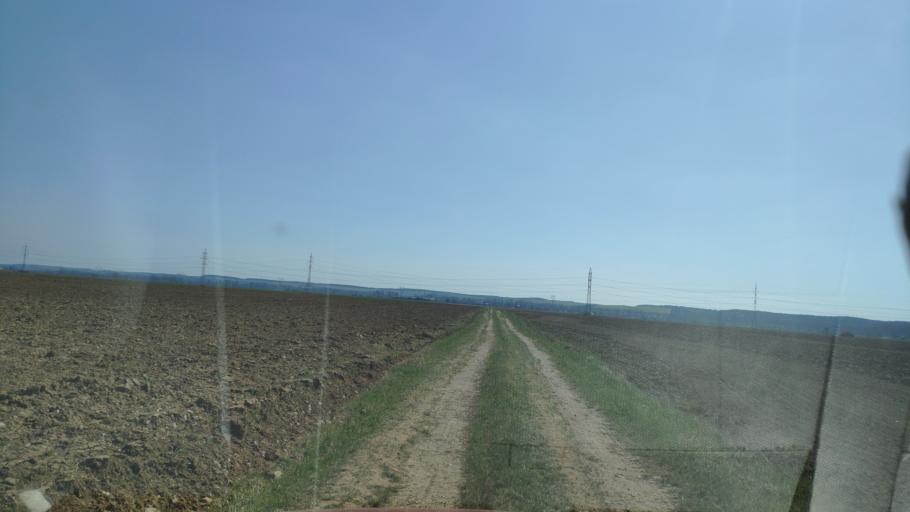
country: SK
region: Kosicky
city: Moldava nad Bodvou
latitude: 48.6023
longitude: 20.9442
